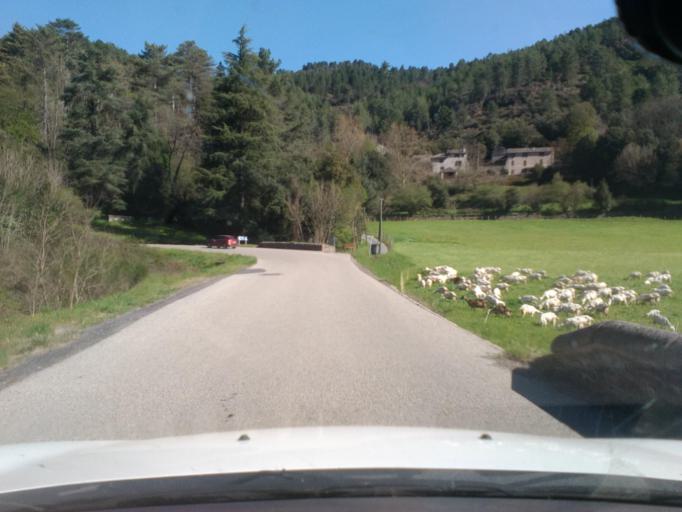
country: FR
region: Languedoc-Roussillon
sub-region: Departement du Gard
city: Saint-Jean-du-Gard
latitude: 44.1704
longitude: 3.7632
